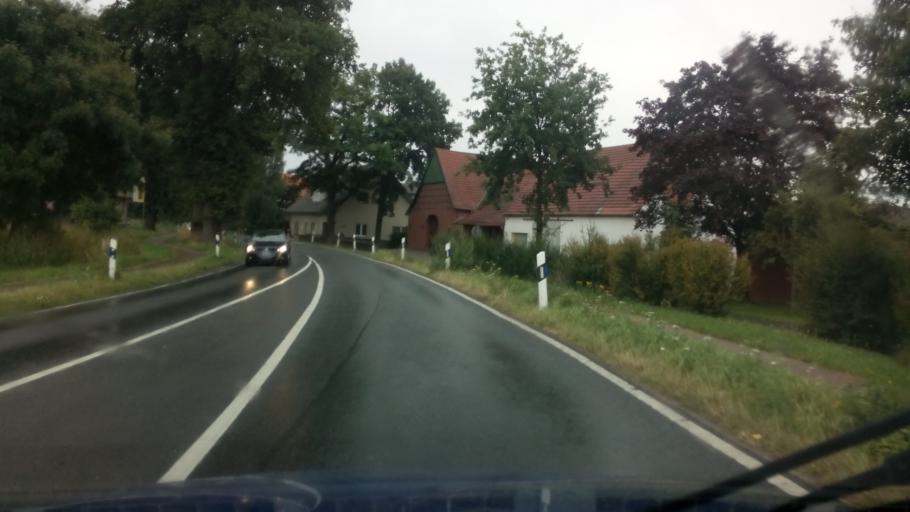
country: DE
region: Lower Saxony
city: Melle
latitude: 52.2124
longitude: 8.3199
